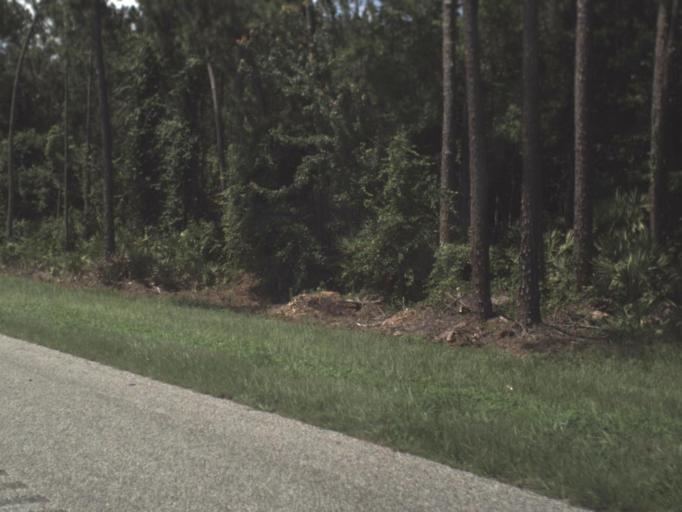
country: US
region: Florida
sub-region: Saint Johns County
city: Saint Augustine Shores
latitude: 29.7746
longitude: -81.3574
